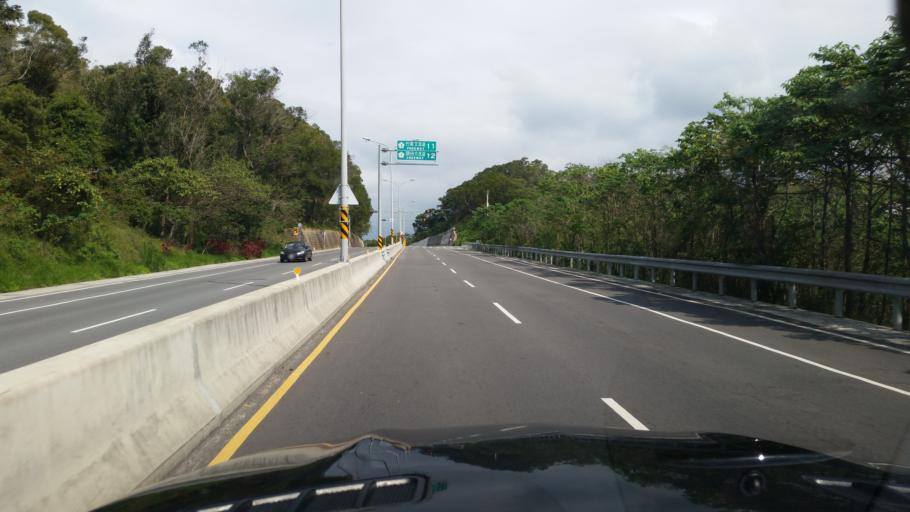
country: TW
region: Taiwan
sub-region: Miaoli
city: Miaoli
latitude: 24.6252
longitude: 120.8506
